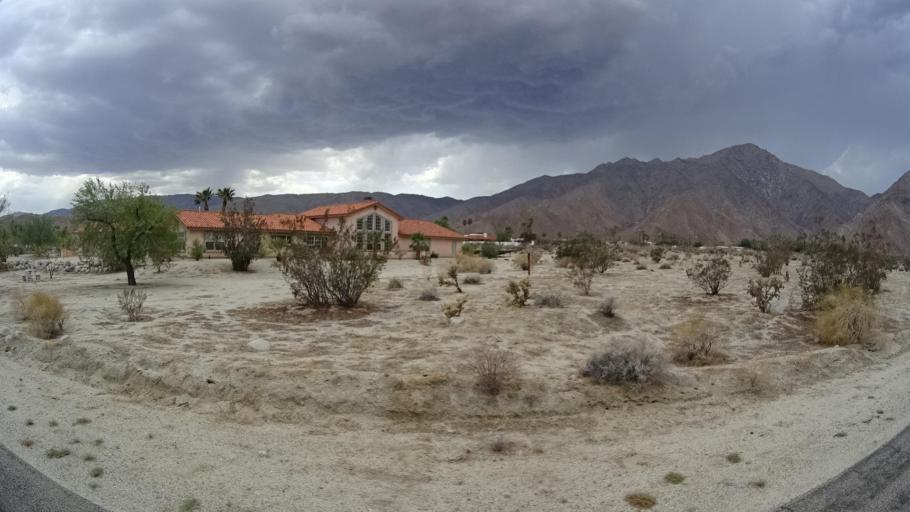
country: US
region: California
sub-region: San Diego County
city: Borrego Springs
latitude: 33.2685
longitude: -116.3948
